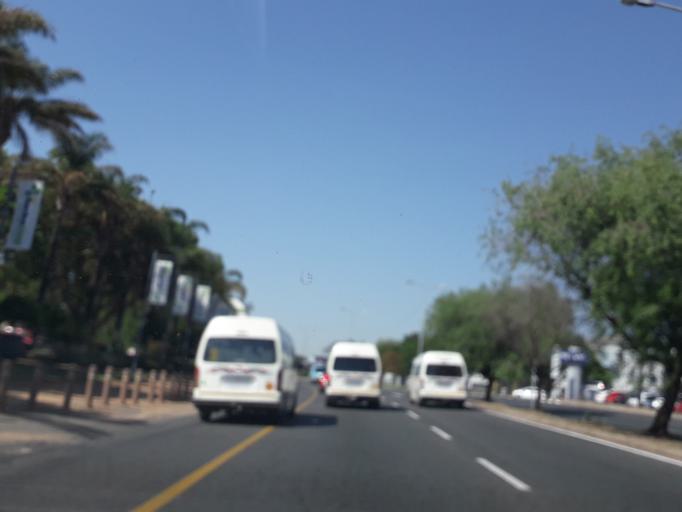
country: ZA
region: Gauteng
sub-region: City of Johannesburg Metropolitan Municipality
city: Johannesburg
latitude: -26.0742
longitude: 28.0130
